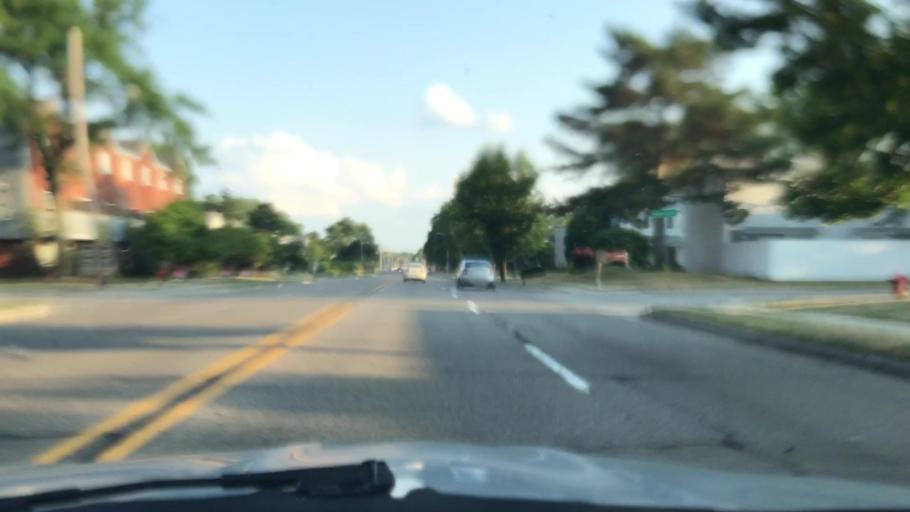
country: US
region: Michigan
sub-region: Oakland County
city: Clawson
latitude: 42.5295
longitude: -83.1654
